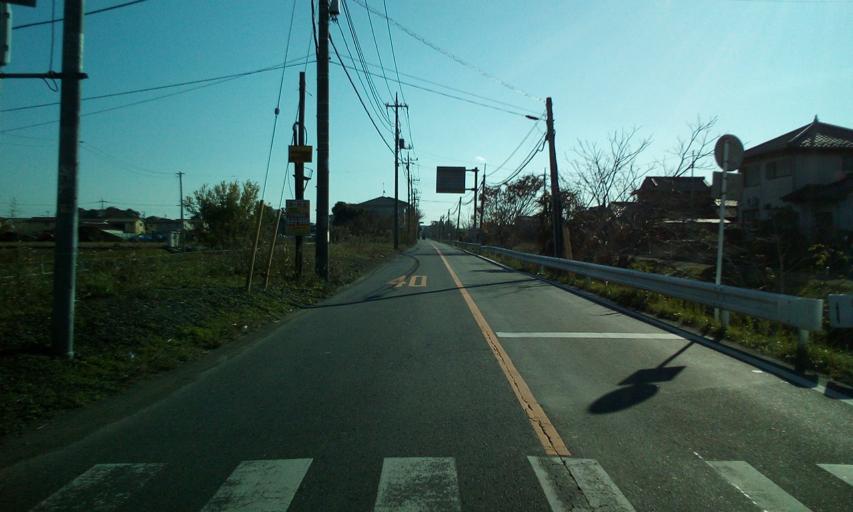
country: JP
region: Saitama
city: Kasukabe
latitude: 35.9894
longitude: 139.7965
